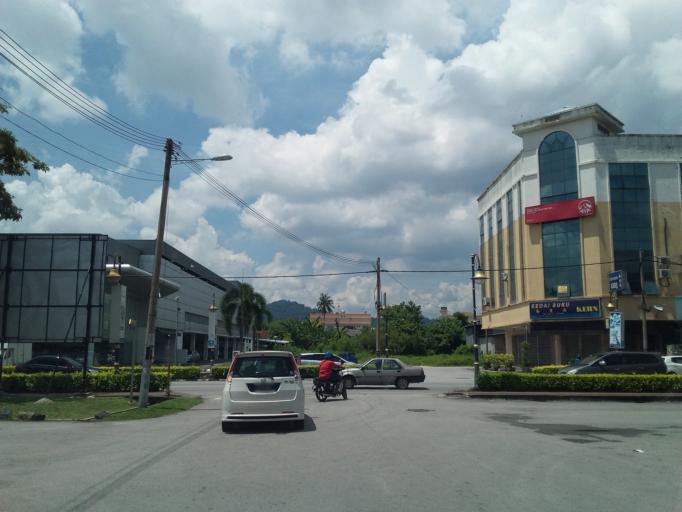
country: MY
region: Johor
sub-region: Daerah Batu Pahat
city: Batu Pahat
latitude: 1.8569
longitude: 102.9264
